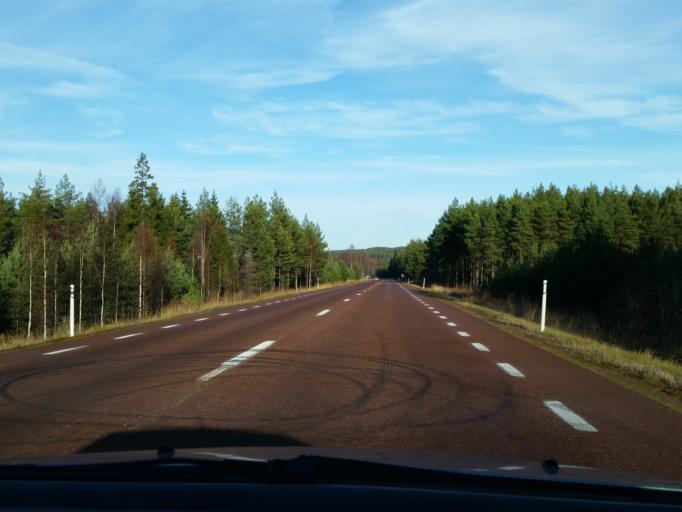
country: AX
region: Alands landsbygd
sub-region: Finstroem
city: Finstroem
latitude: 60.2891
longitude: 19.9531
